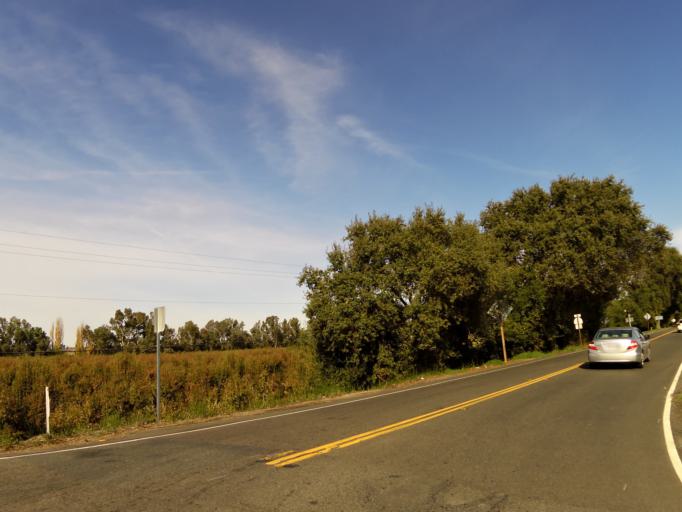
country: US
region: California
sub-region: Solano County
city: Rio Vista
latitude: 38.1724
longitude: -121.5948
